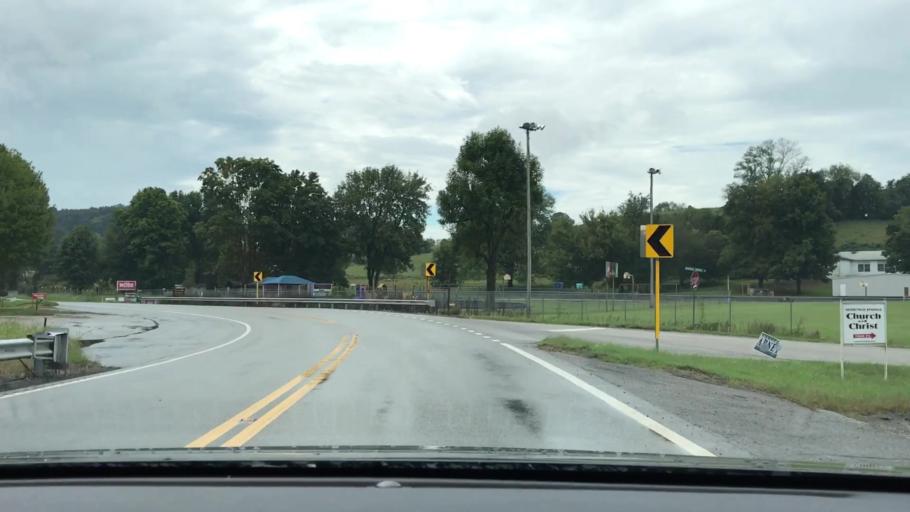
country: US
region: Tennessee
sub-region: Macon County
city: Red Boiling Springs
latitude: 36.5757
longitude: -85.7805
